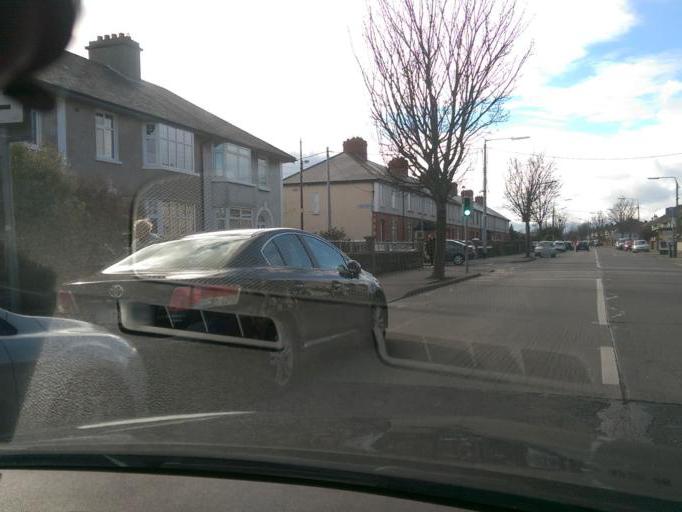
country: IE
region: Leinster
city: Marino
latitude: 53.3771
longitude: -6.2243
